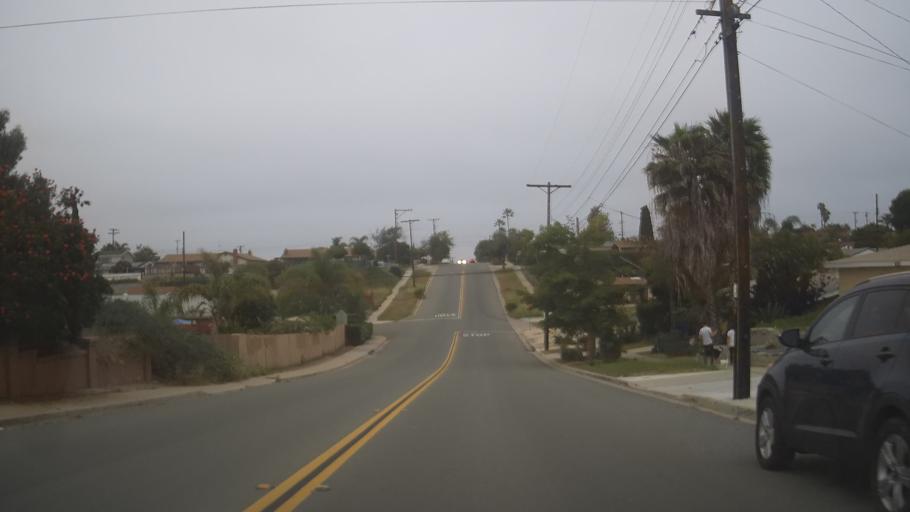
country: US
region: California
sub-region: San Diego County
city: Bonita
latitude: 32.6224
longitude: -117.0476
